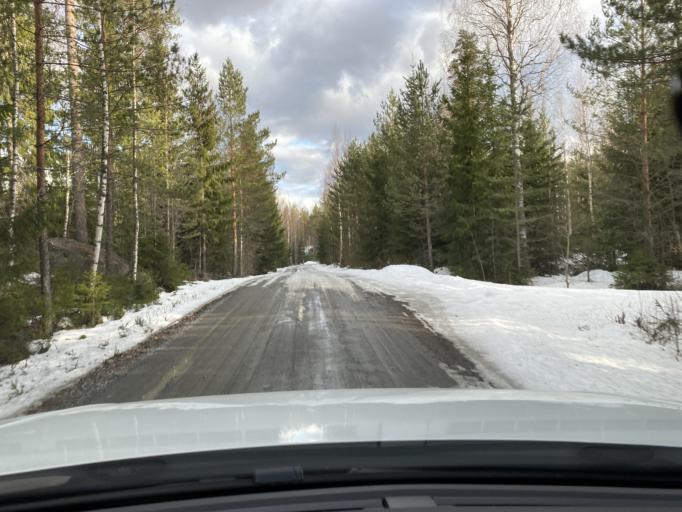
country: FI
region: Pirkanmaa
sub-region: Lounais-Pirkanmaa
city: Mouhijaervi
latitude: 61.4333
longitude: 22.9869
